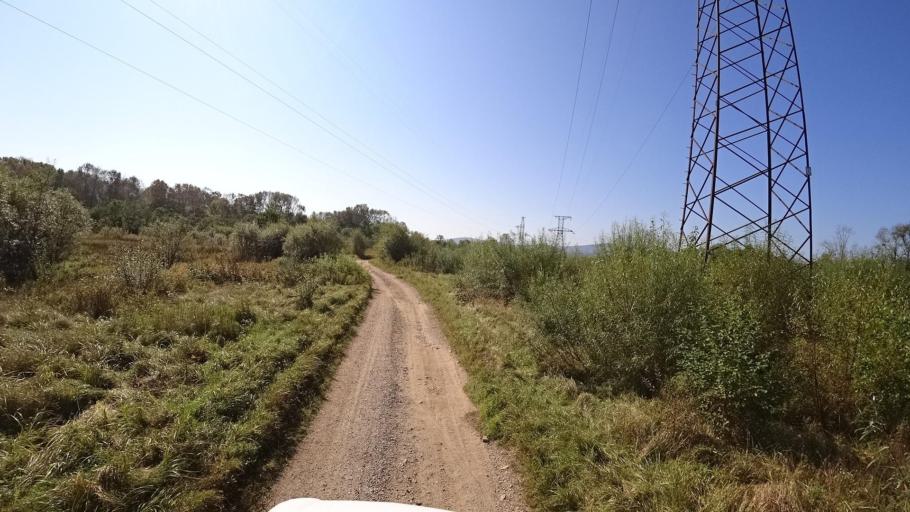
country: RU
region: Jewish Autonomous Oblast
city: Bira
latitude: 49.0007
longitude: 132.4767
